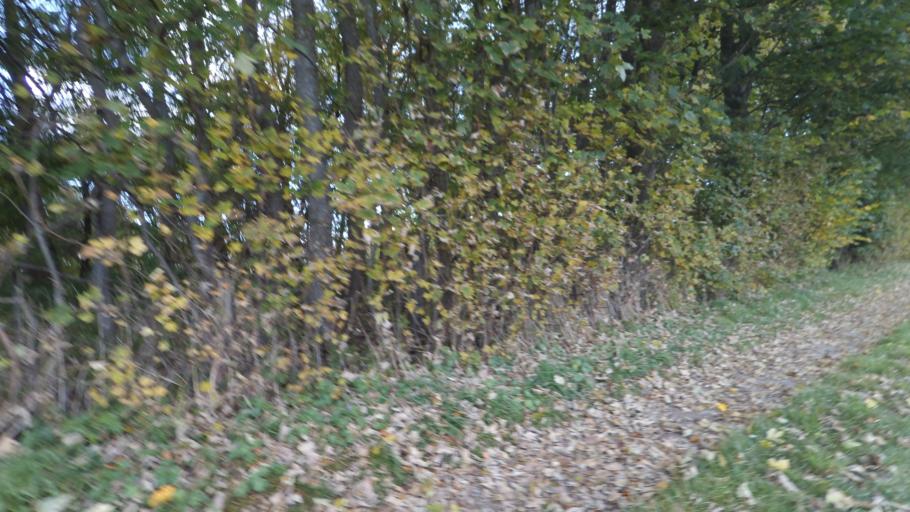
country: DK
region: Central Jutland
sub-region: Arhus Kommune
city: Kolt
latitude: 56.1297
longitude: 10.0901
